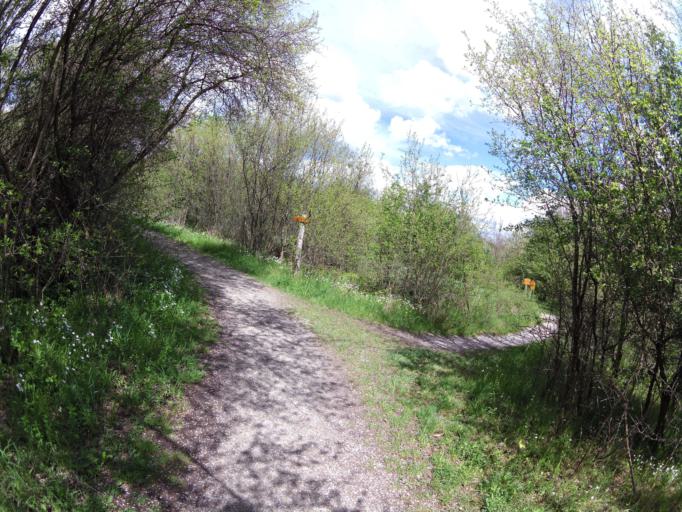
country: DE
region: Thuringia
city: Weberstedt
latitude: 51.0958
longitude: 10.5147
